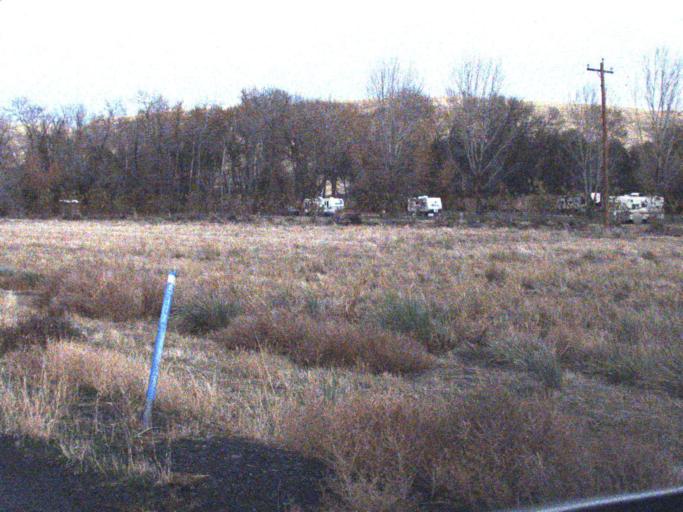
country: US
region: Washington
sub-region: Columbia County
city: Dayton
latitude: 46.5073
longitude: -118.0523
